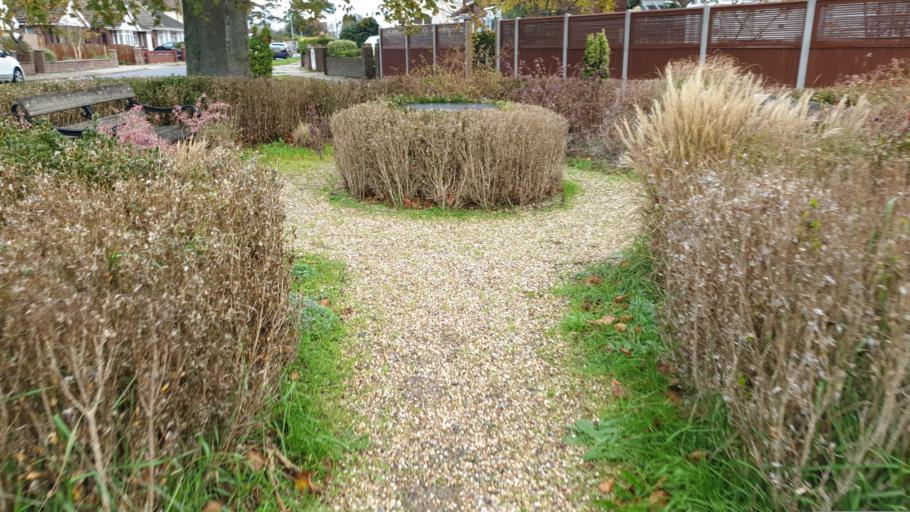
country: GB
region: England
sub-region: Essex
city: Clacton-on-Sea
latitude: 51.7943
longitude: 1.1649
